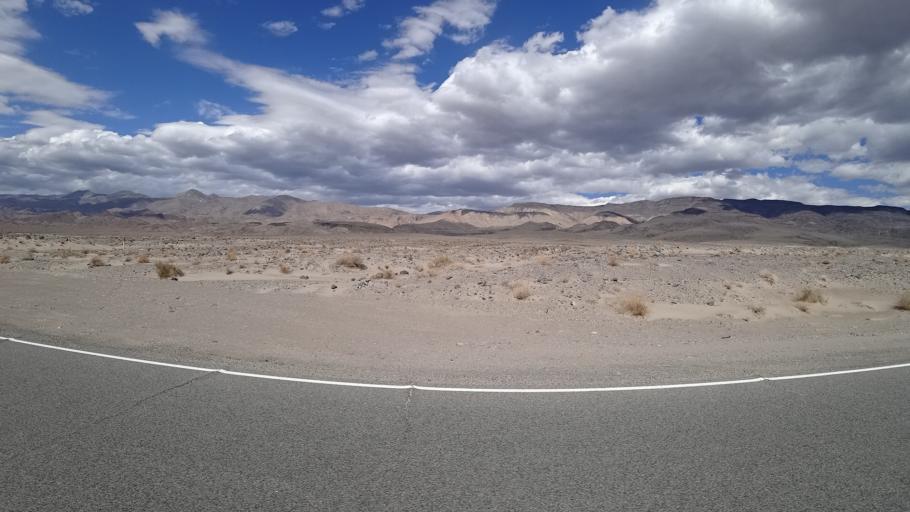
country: US
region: California
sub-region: Inyo County
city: Lone Pine
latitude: 36.4373
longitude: -117.8296
